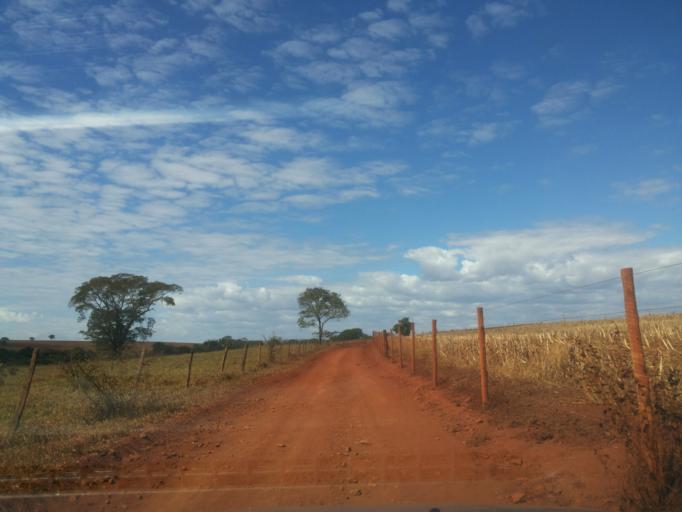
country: BR
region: Minas Gerais
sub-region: Centralina
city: Centralina
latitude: -18.5529
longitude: -49.2380
